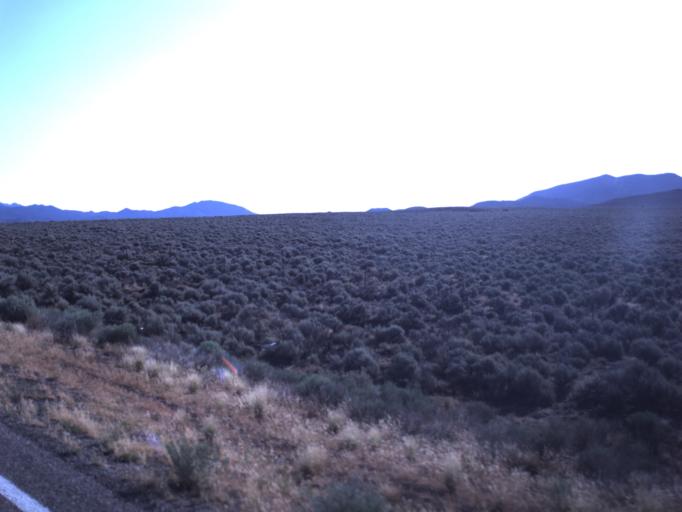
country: US
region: Utah
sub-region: Beaver County
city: Milford
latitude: 38.1602
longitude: -112.9564
